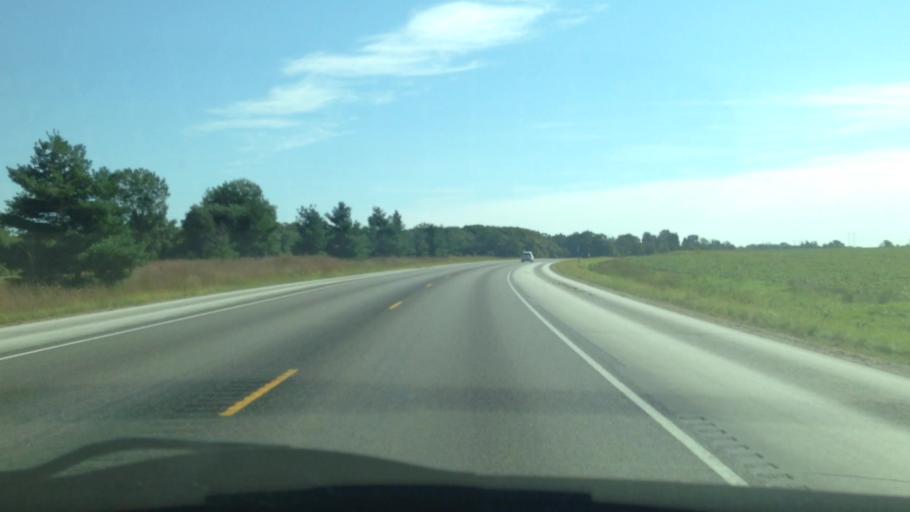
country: US
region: Minnesota
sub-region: Fillmore County
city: Harmony
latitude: 43.5555
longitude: -91.9740
